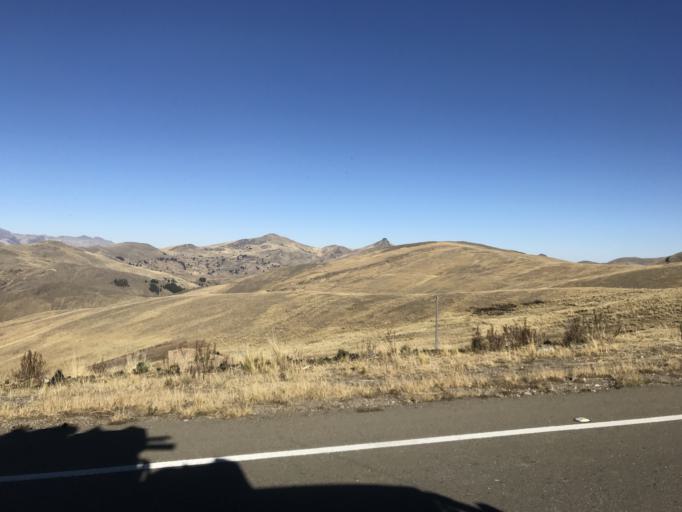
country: PE
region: Puno
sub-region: Yunguyo
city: Yunguyo
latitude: -16.1699
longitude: -68.9839
